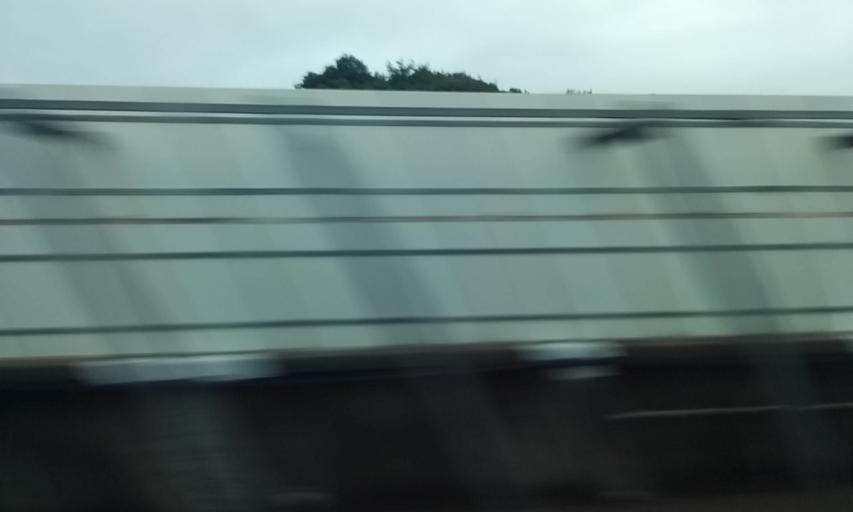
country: JP
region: Hyogo
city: Tatsunocho-tominaga
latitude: 34.8284
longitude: 134.6064
